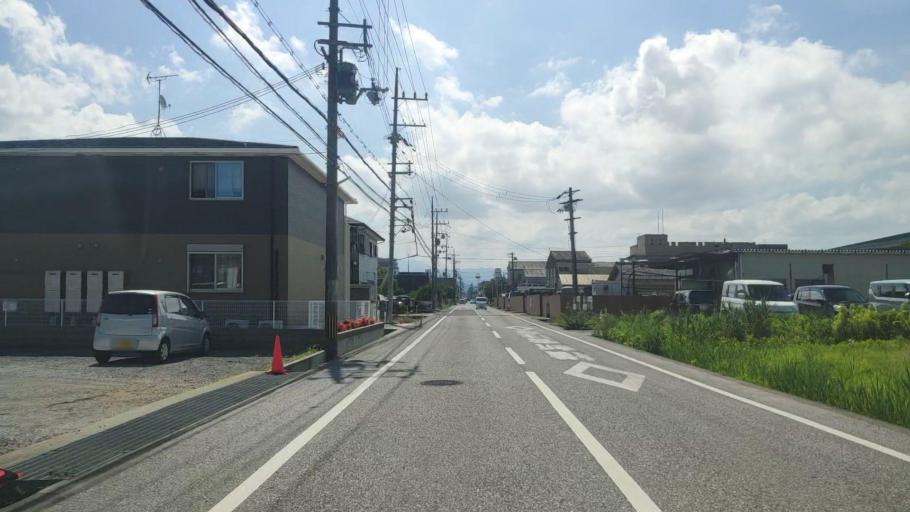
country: JP
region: Shiga Prefecture
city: Hikone
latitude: 35.2627
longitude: 136.2354
